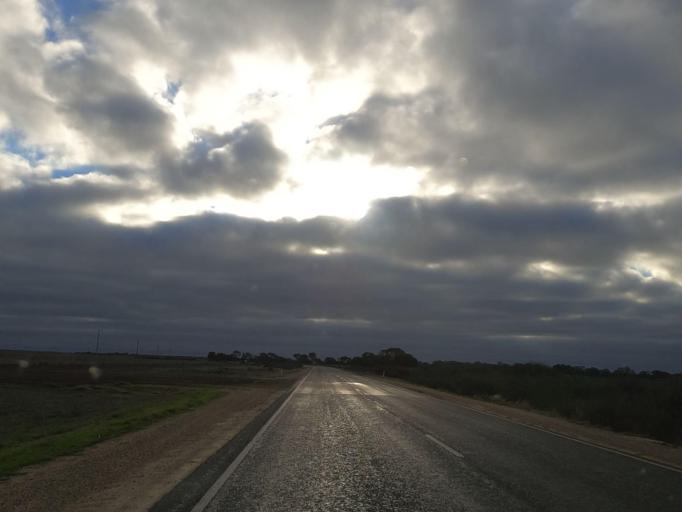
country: AU
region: Victoria
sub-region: Swan Hill
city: Swan Hill
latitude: -35.6530
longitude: 143.8468
